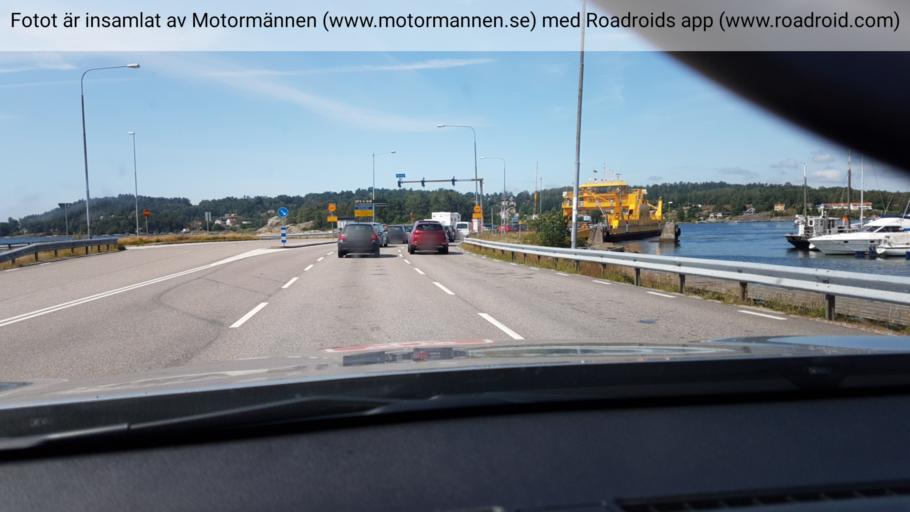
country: SE
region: Vaestra Goetaland
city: Svanesund
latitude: 58.1345
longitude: 11.8420
